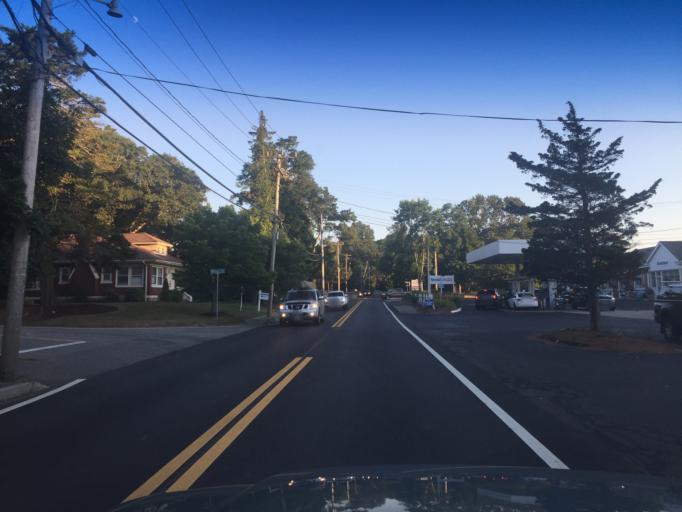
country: US
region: Massachusetts
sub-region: Barnstable County
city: Falmouth
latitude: 41.5615
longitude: -70.6191
